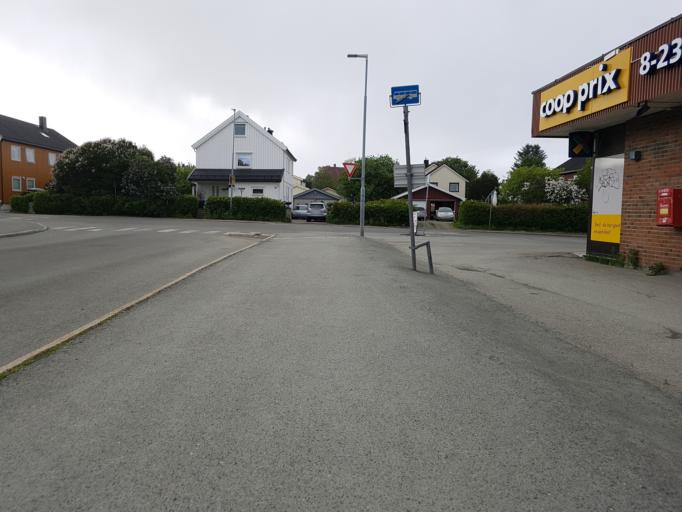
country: NO
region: Sor-Trondelag
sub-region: Trondheim
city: Trondheim
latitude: 63.4329
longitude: 10.4471
